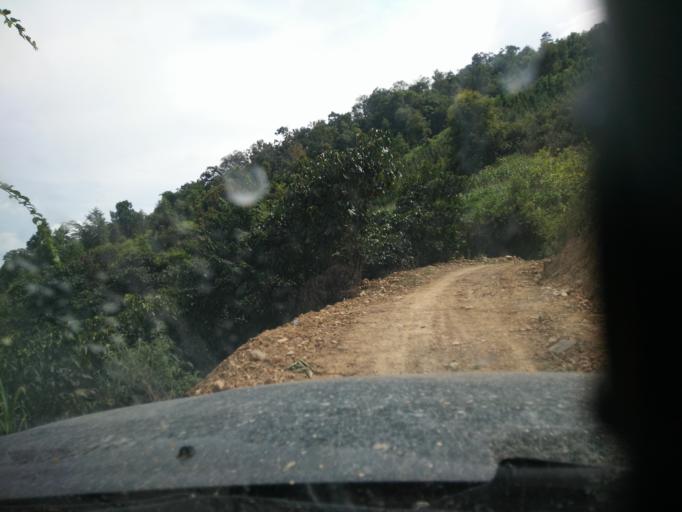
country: CN
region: Guangxi Zhuangzu Zizhiqu
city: Leli
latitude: 24.7700
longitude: 105.9036
